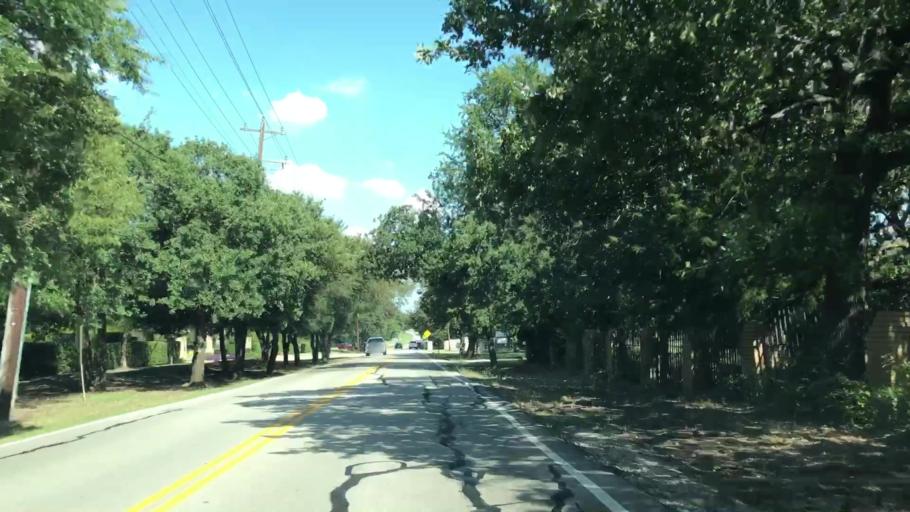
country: US
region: Texas
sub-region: Tarrant County
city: Keller
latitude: 32.9076
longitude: -97.2219
